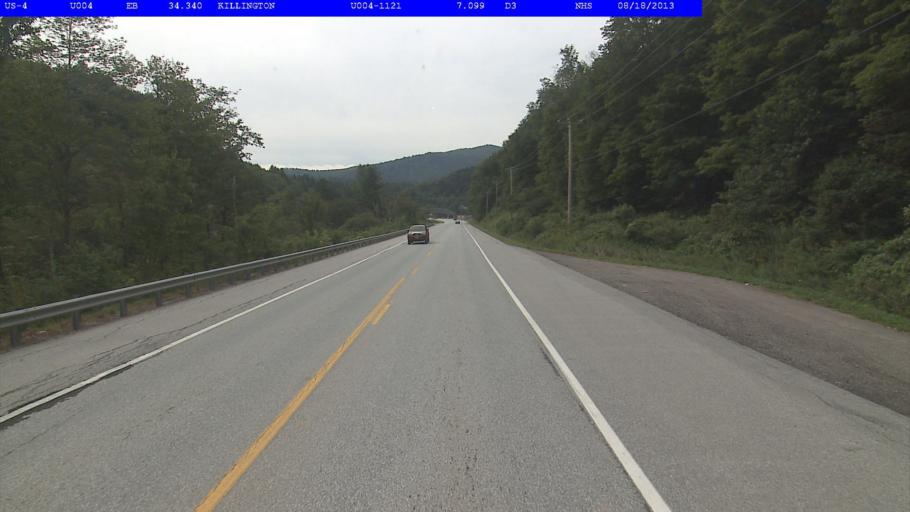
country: US
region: Vermont
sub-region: Rutland County
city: Rutland
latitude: 43.6187
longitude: -72.7588
